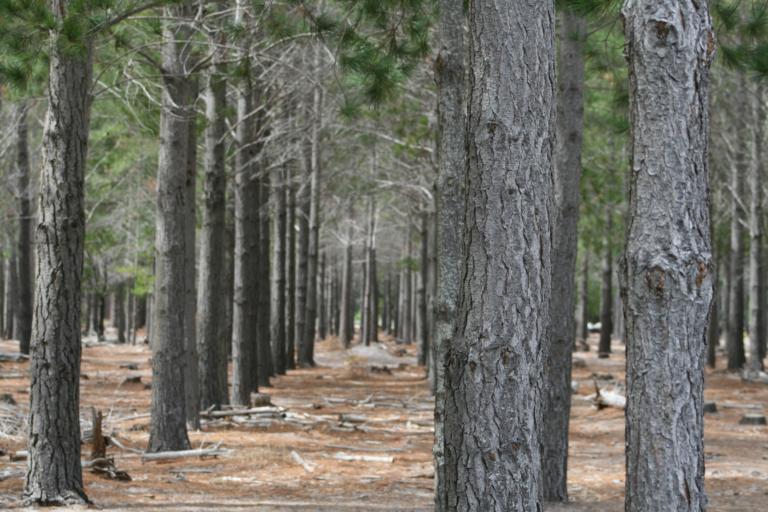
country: ZA
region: Western Cape
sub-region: City of Cape Town
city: Bergvliet
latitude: -34.0557
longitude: 18.4369
